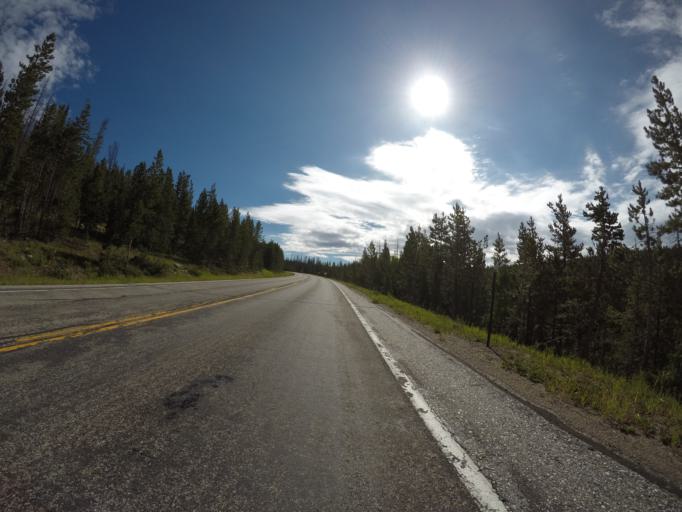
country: US
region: Wyoming
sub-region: Carbon County
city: Saratoga
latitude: 41.3238
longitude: -106.4488
